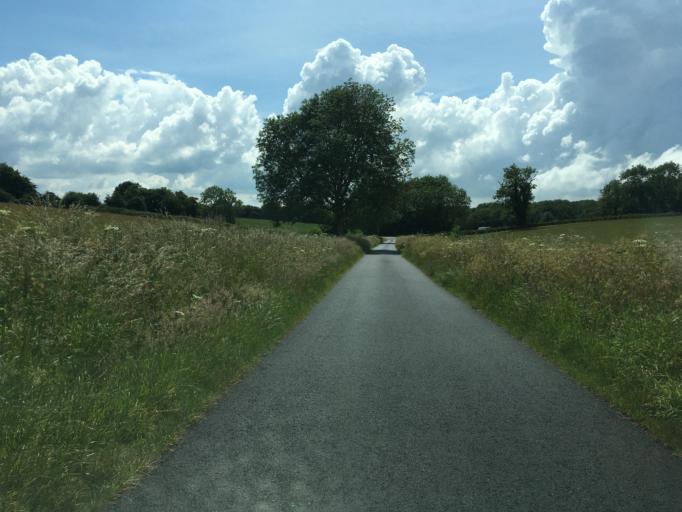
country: GB
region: England
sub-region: Gloucestershire
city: Tetbury
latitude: 51.6250
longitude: -2.2169
